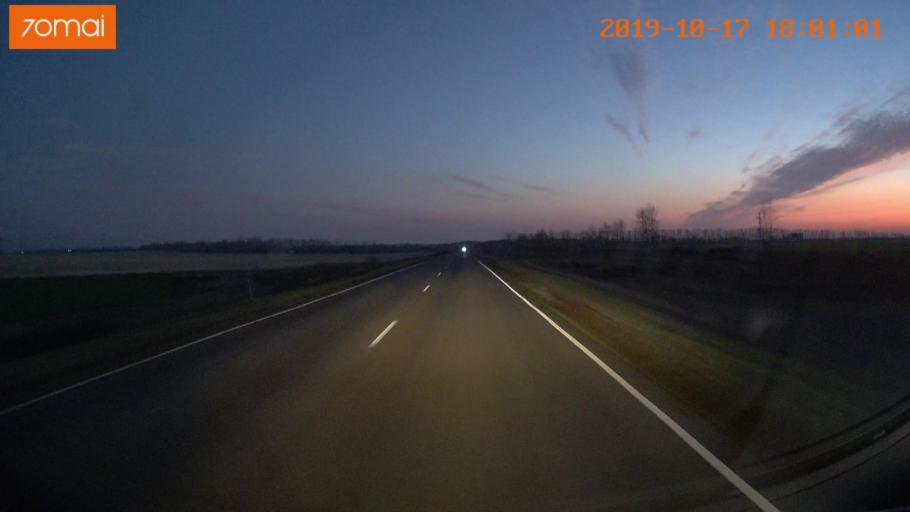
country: RU
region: Tula
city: Kurkino
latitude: 53.5135
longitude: 38.6126
